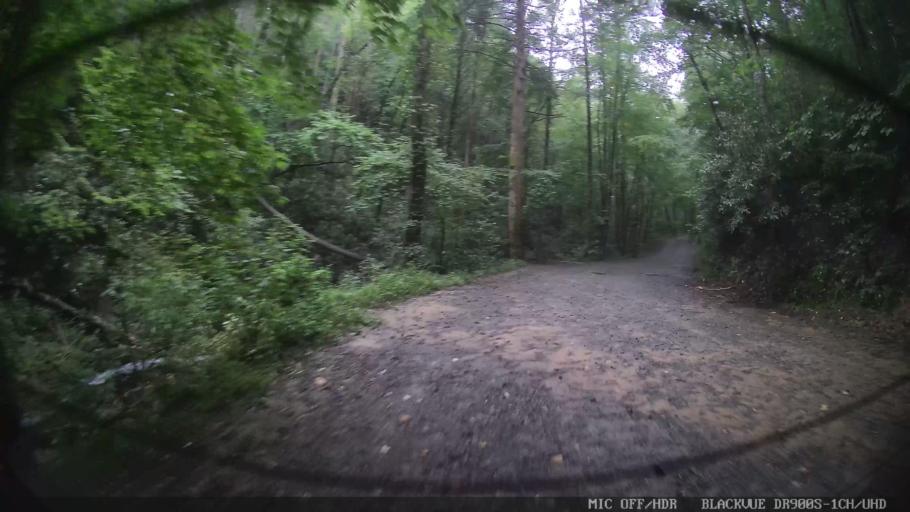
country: US
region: Georgia
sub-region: Gilmer County
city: Ellijay
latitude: 34.8183
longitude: -84.5643
